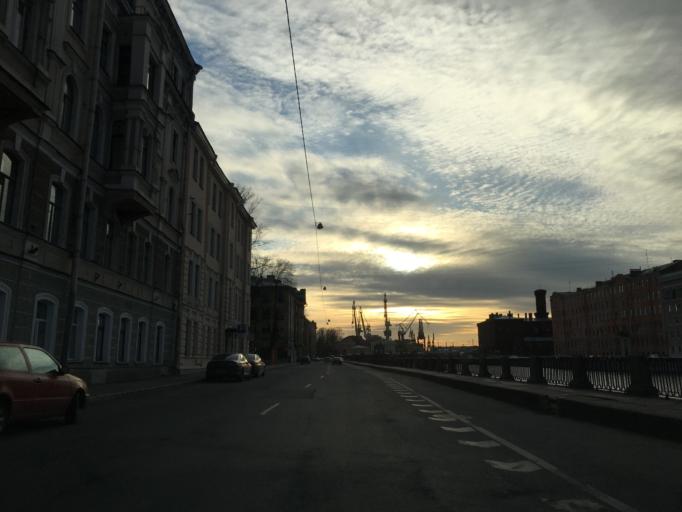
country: RU
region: St.-Petersburg
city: Admiralteisky
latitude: 59.9158
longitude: 30.2862
